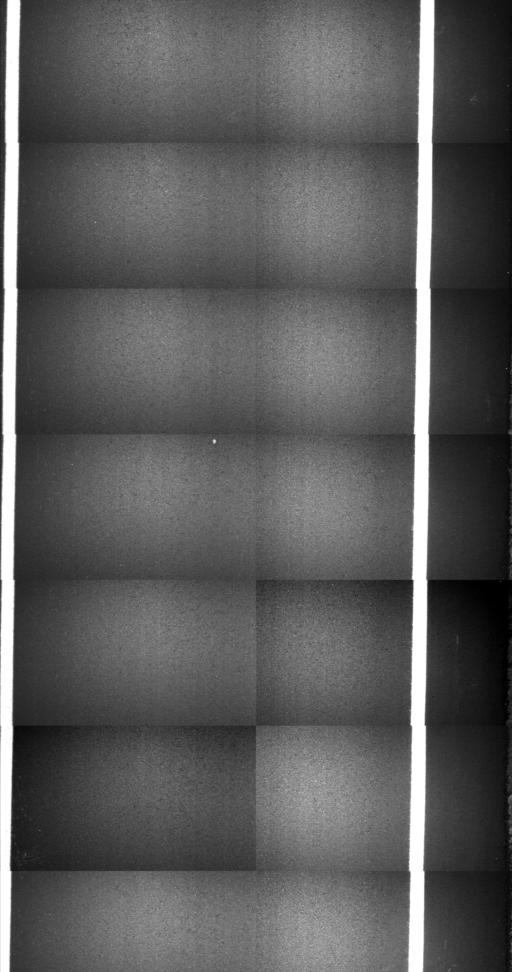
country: US
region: Vermont
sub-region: Caledonia County
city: Lyndonville
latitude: 44.6175
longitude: -71.9080
